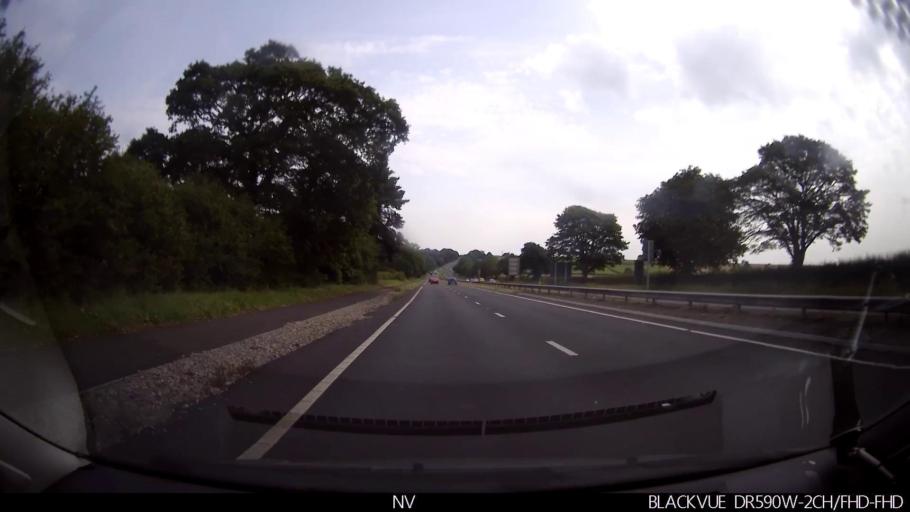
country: GB
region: England
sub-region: North Yorkshire
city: Huttons Ambo
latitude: 54.0746
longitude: -0.9116
